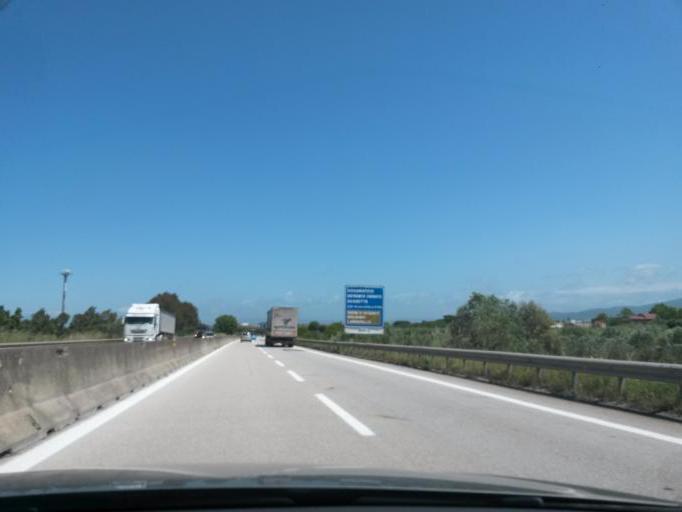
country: IT
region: Tuscany
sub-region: Provincia di Livorno
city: Donoratico
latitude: 43.1718
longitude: 10.5632
